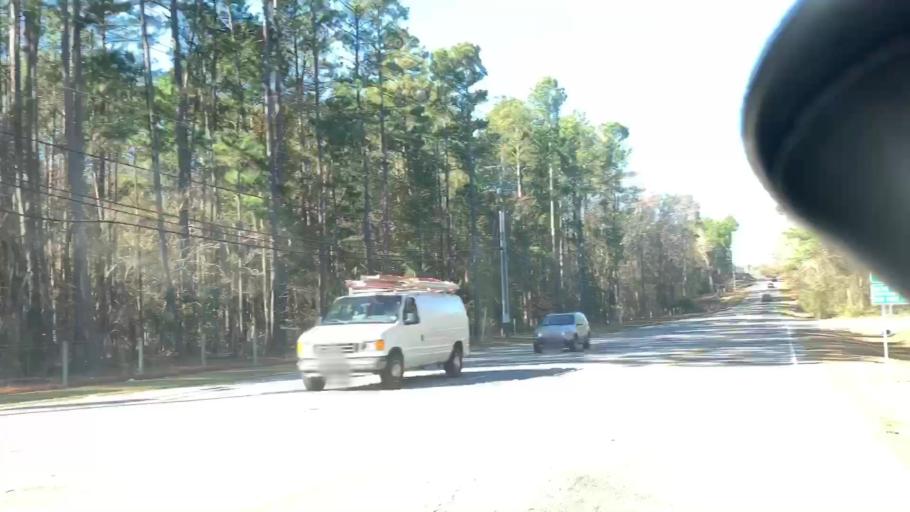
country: US
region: South Carolina
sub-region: Richland County
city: Woodfield
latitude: 34.0722
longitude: -80.9155
